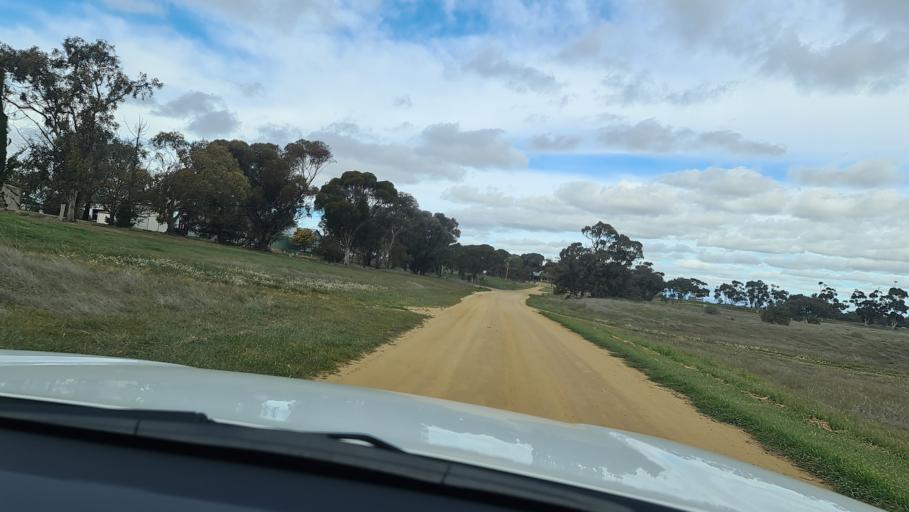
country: AU
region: Victoria
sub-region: Horsham
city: Horsham
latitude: -36.6215
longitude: 142.4204
